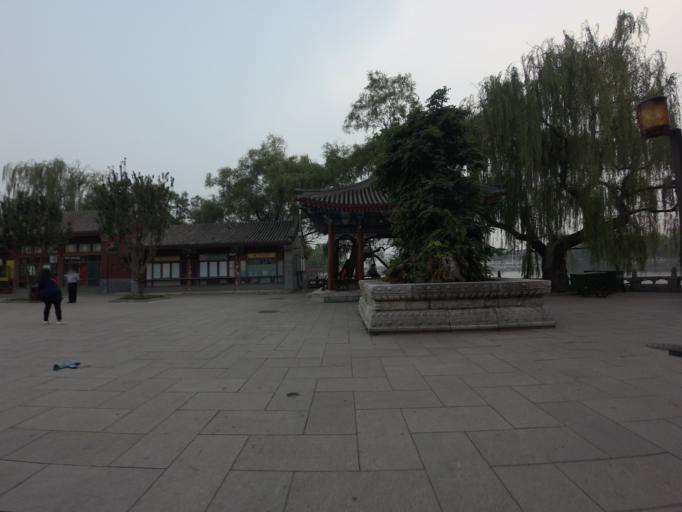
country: CN
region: Beijing
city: Beijing
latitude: 39.9230
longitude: 116.3821
